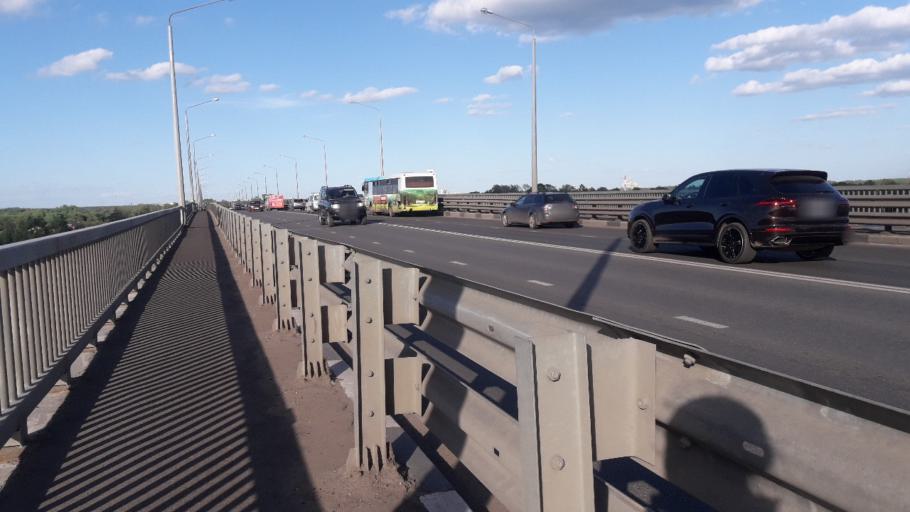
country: RU
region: Jaroslavl
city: Yaroslavl
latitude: 57.6404
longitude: 39.8917
